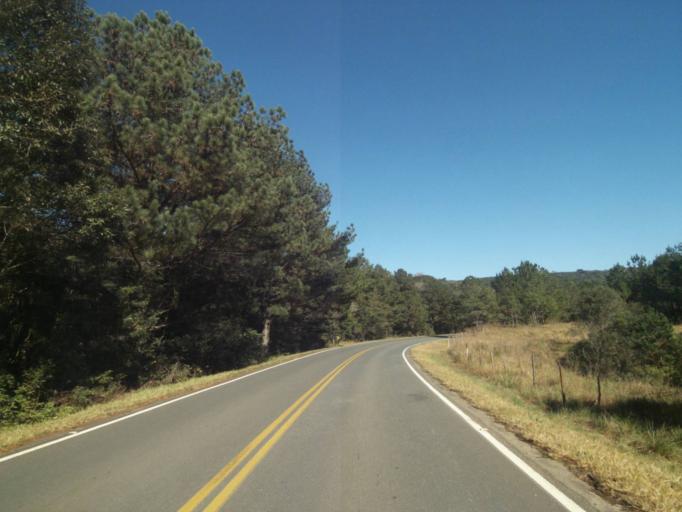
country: BR
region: Parana
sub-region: Telemaco Borba
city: Telemaco Borba
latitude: -24.4240
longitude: -50.5804
